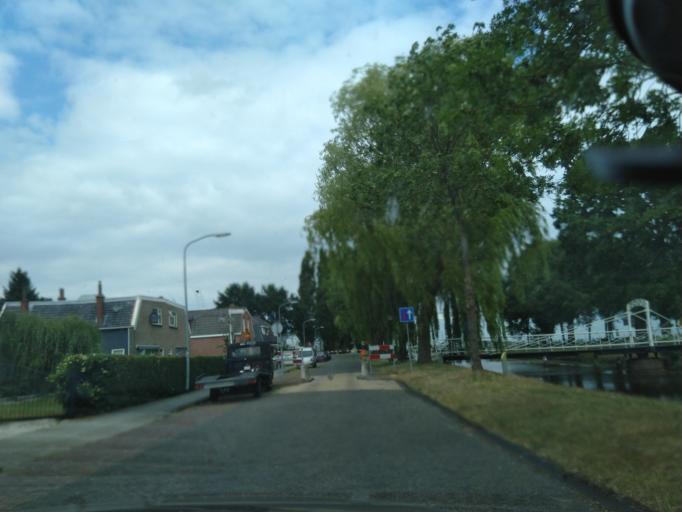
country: NL
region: Groningen
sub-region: Gemeente Pekela
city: Oude Pekela
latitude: 53.1116
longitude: 7.0245
